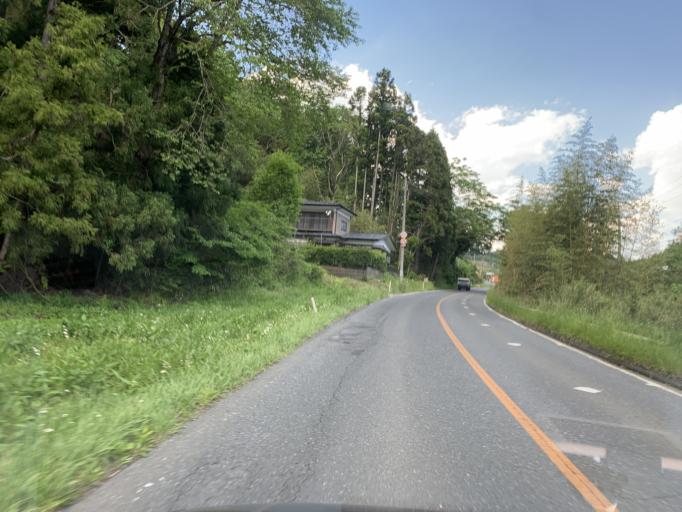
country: JP
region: Miyagi
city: Wakuya
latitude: 38.5590
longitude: 141.1361
